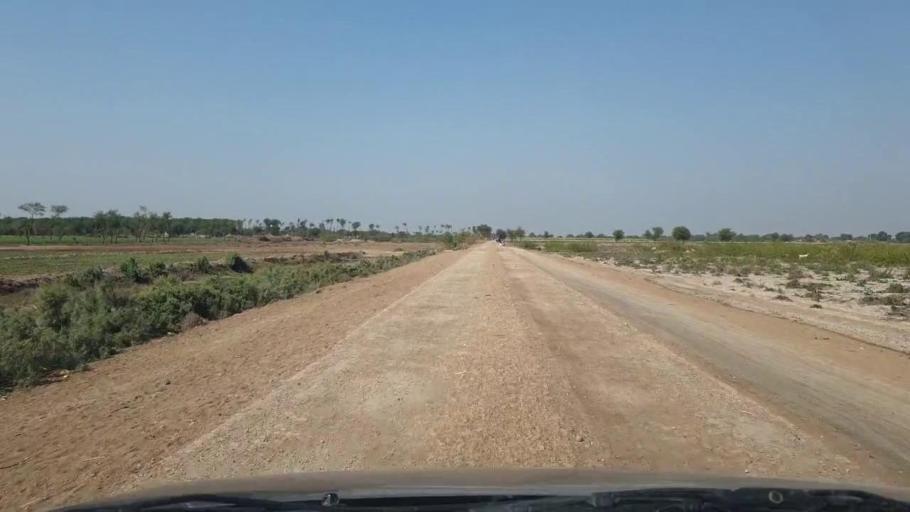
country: PK
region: Sindh
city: Samaro
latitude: 25.2324
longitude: 69.2795
